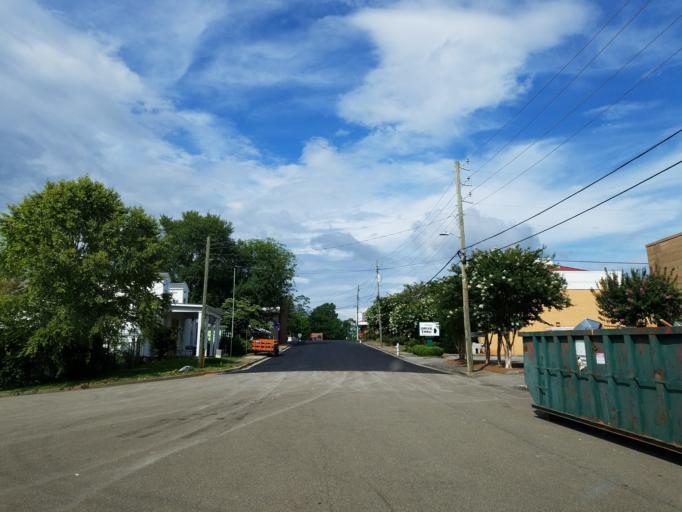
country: US
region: Georgia
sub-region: Pickens County
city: Jasper
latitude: 34.4691
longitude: -84.4325
